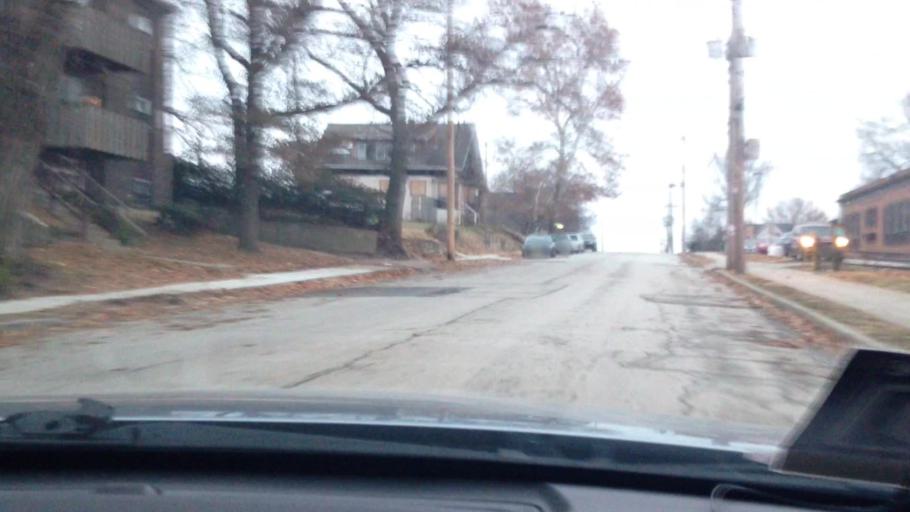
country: US
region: Missouri
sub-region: Clay County
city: North Kansas City
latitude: 39.1092
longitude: -94.5600
